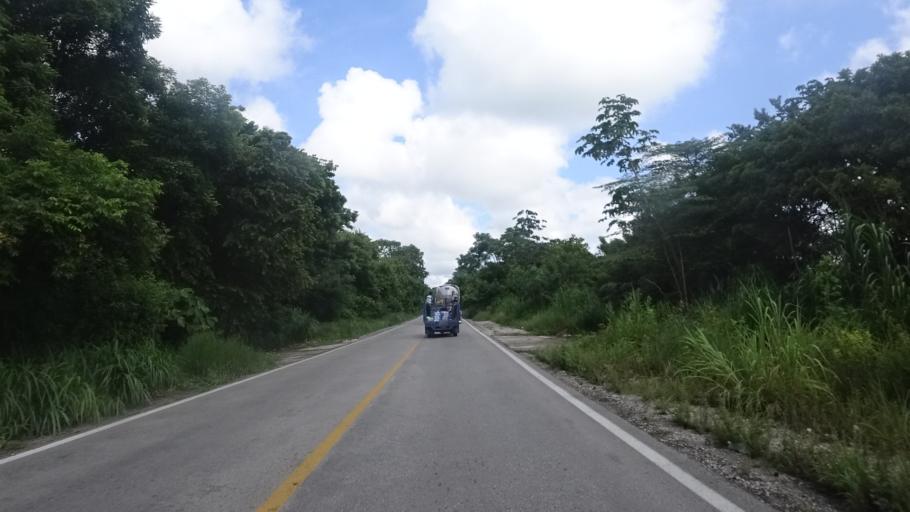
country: MX
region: Chiapas
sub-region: Catazaja
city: Catazaja
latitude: 17.6144
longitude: -92.0253
